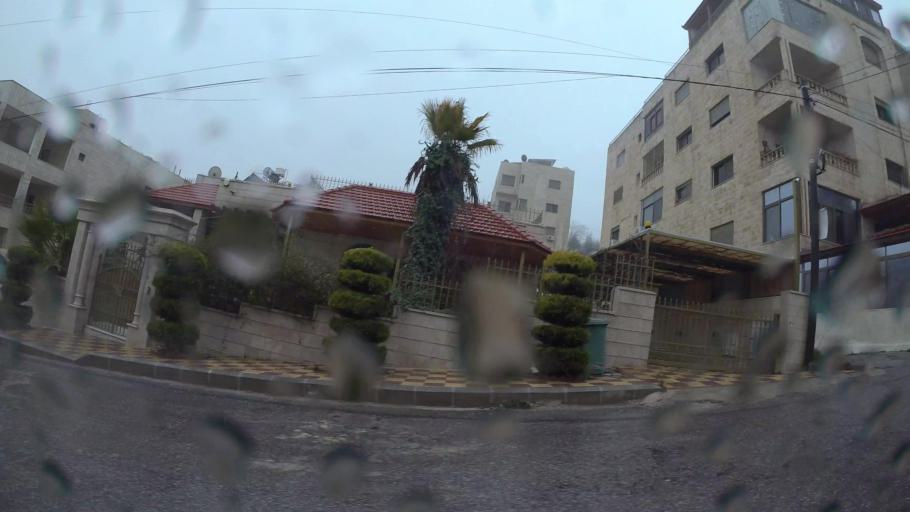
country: JO
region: Amman
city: Al Jubayhah
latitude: 32.0130
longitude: 35.8859
